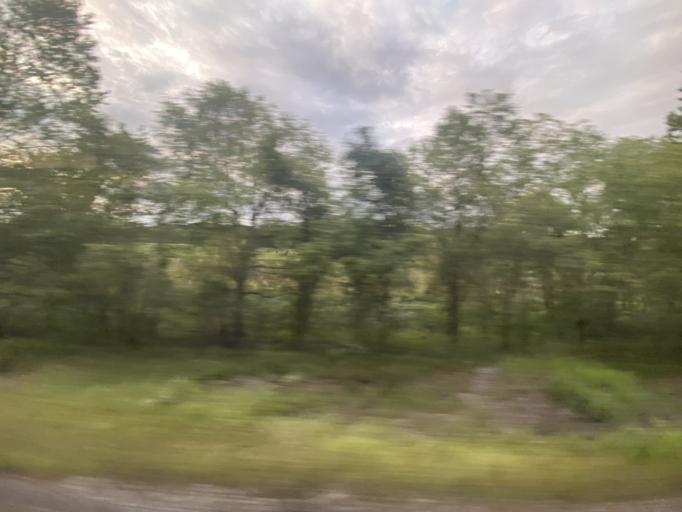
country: US
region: West Virginia
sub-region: Mineral County
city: Fort Ashby
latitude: 39.5178
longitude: -78.5547
